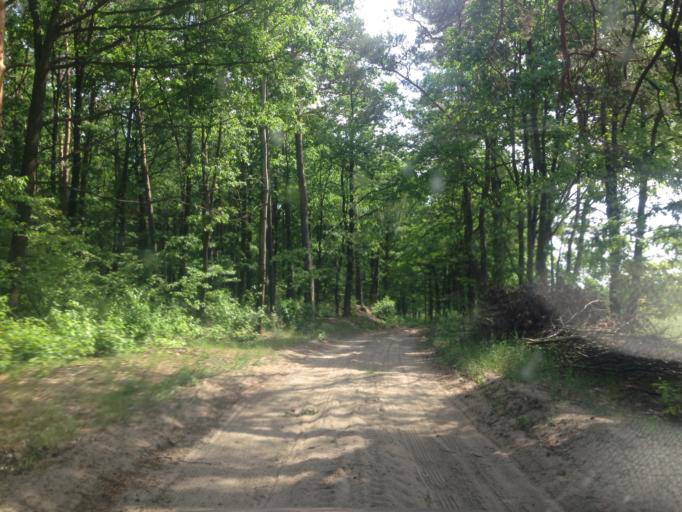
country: PL
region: Kujawsko-Pomorskie
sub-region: Powiat brodnicki
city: Gorzno
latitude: 53.1788
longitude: 19.6493
